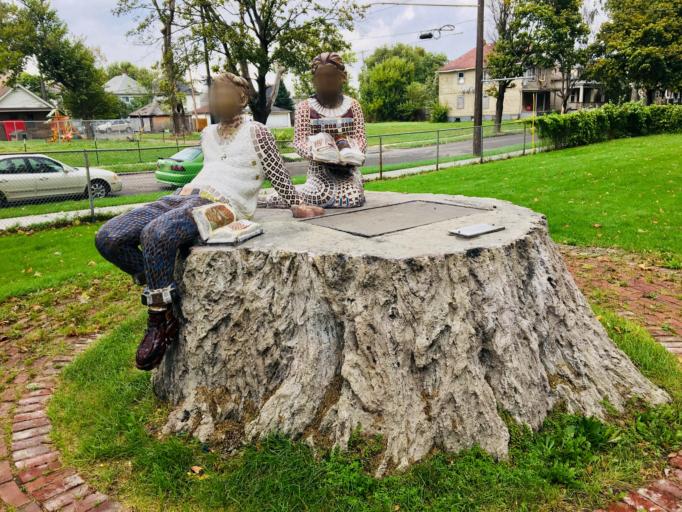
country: US
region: Michigan
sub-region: Wayne County
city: Dearborn
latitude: 42.3321
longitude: -83.1276
